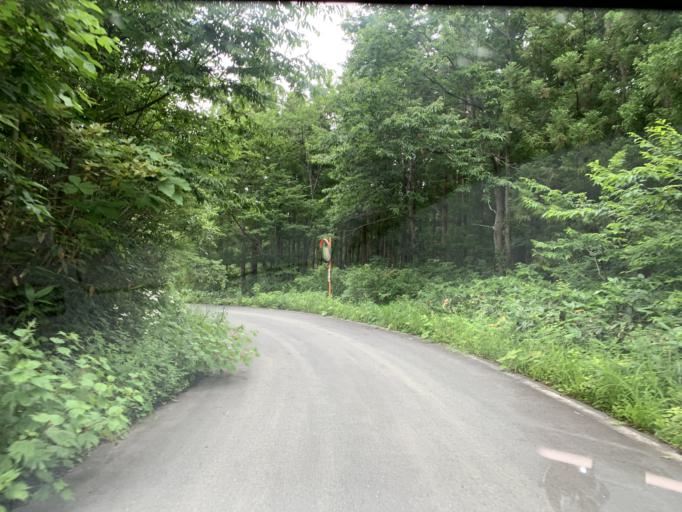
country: JP
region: Iwate
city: Ichinoseki
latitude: 38.9573
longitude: 140.8899
